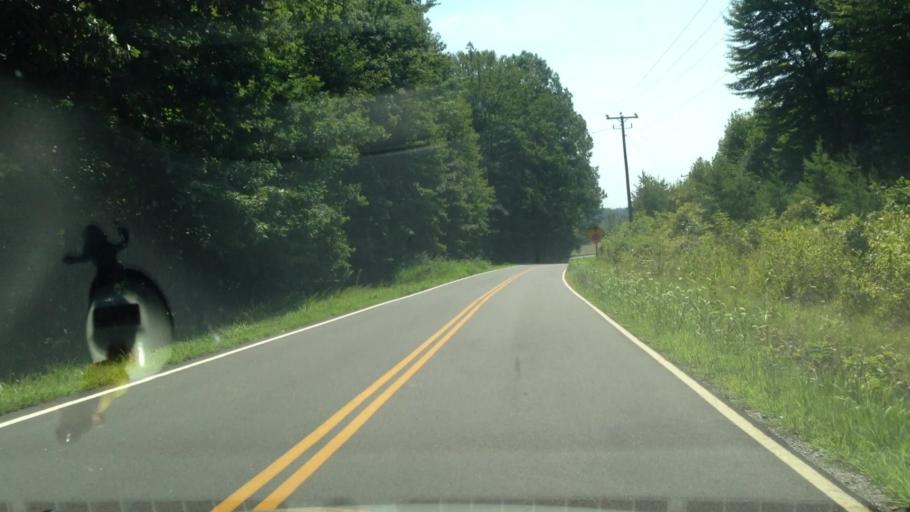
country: US
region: Virginia
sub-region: Patrick County
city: Patrick Springs
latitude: 36.6020
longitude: -80.1640
